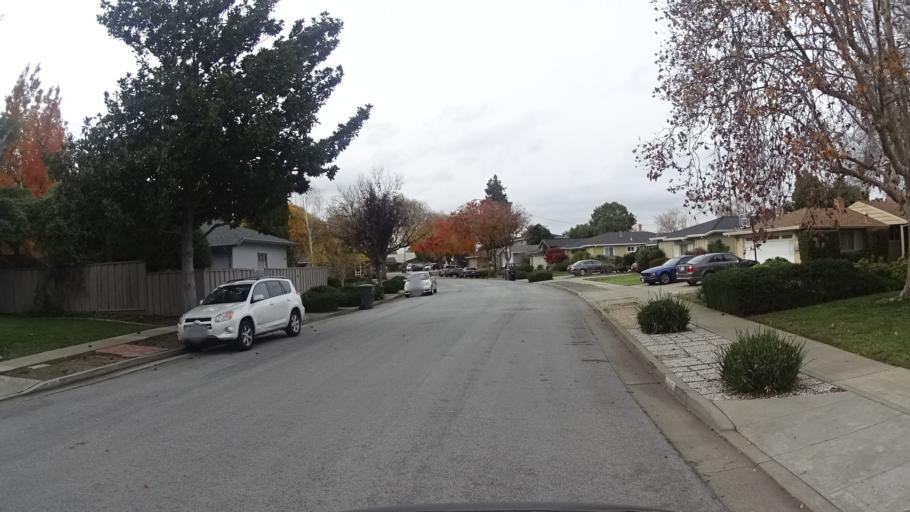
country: US
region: California
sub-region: Santa Clara County
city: Sunnyvale
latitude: 37.3707
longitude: -122.0545
